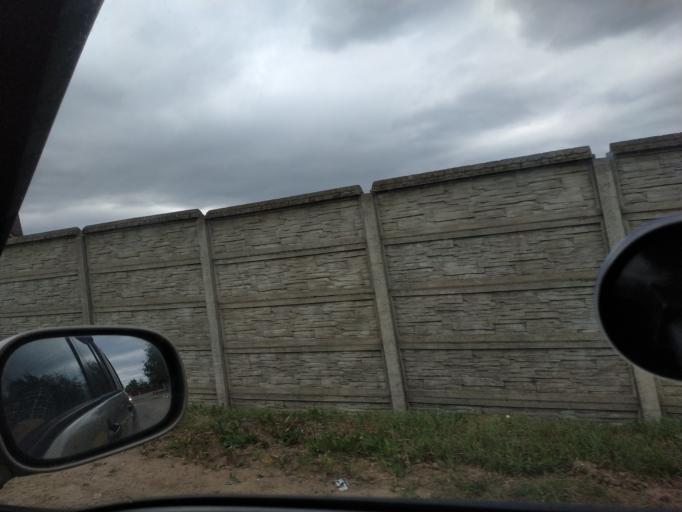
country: RU
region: Moskovskaya
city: Chernogolovka
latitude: 56.0665
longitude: 38.2655
